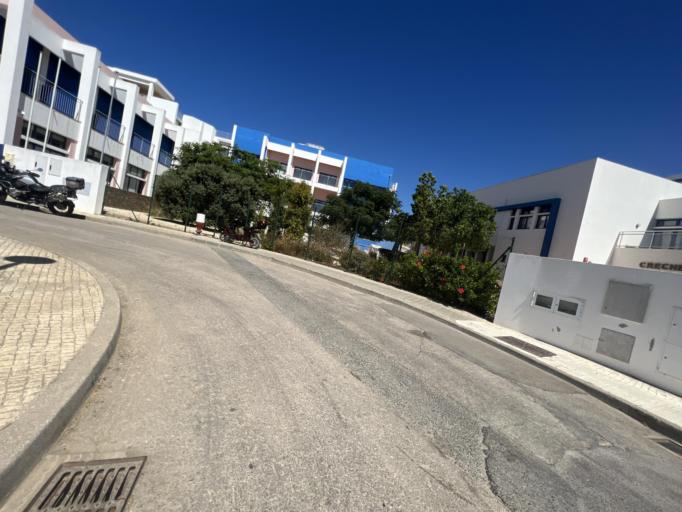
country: PT
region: Faro
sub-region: Portimao
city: Portimao
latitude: 37.1290
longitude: -8.5109
